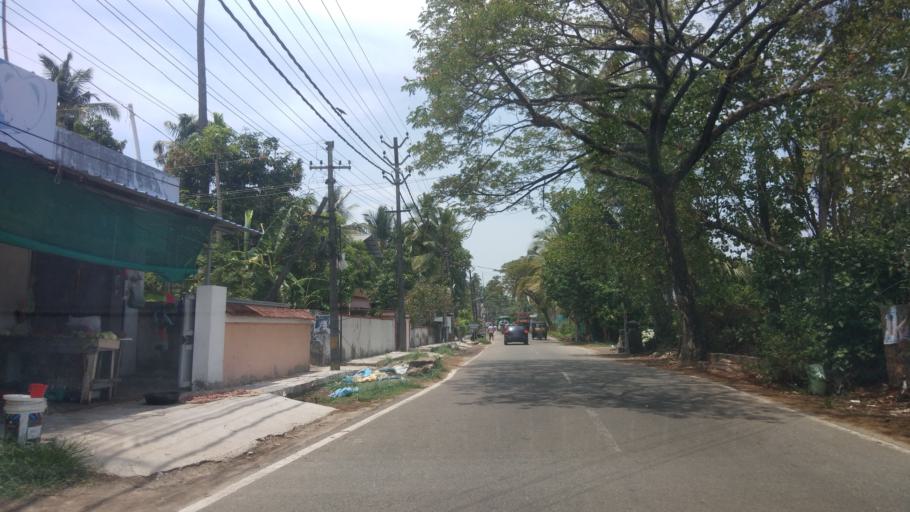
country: IN
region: Kerala
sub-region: Ernakulam
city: Cochin
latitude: 9.8917
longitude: 76.2593
